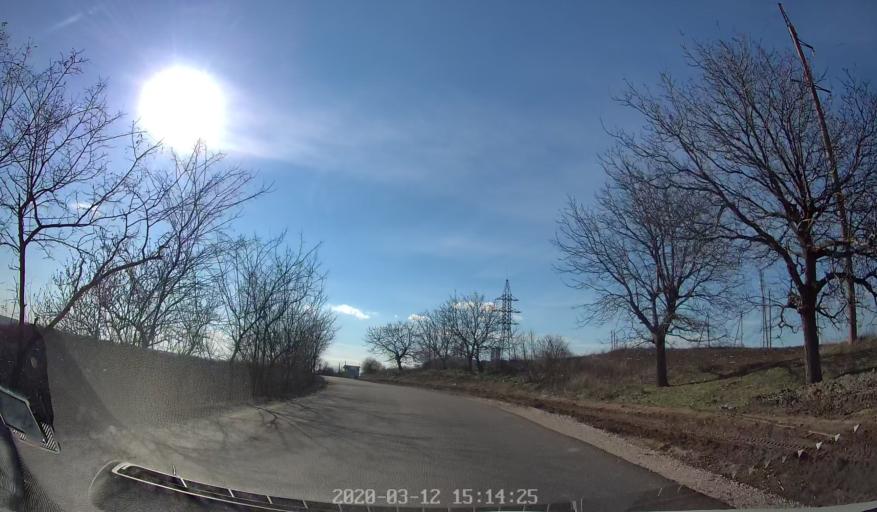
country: MD
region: Chisinau
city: Ciorescu
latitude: 47.2352
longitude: 28.9512
